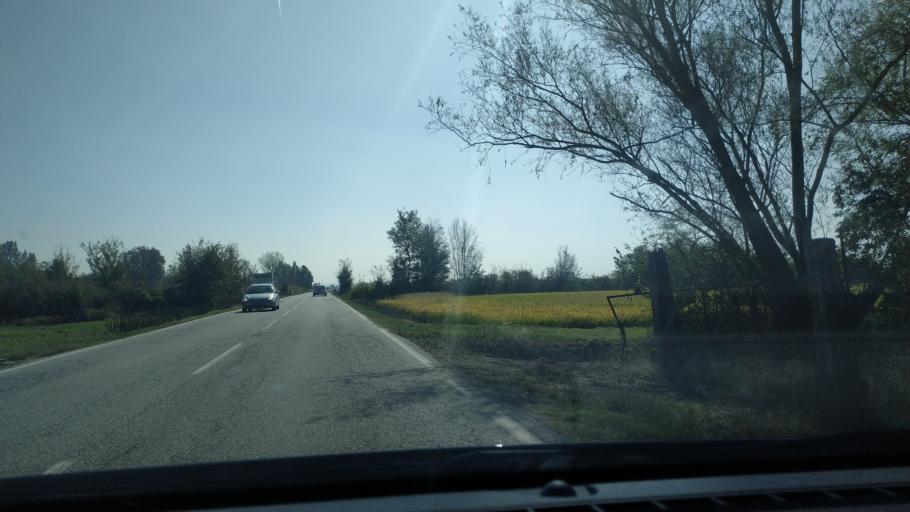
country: IT
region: Piedmont
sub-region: Provincia di Alessandria
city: Borgo San Martino
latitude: 45.1088
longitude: 8.5129
